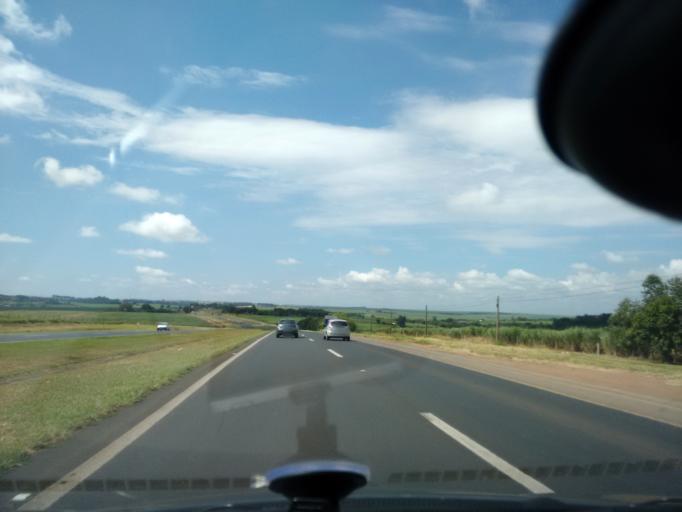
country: BR
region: Sao Paulo
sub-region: Ibate
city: Ibate
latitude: -21.9597
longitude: -47.9804
